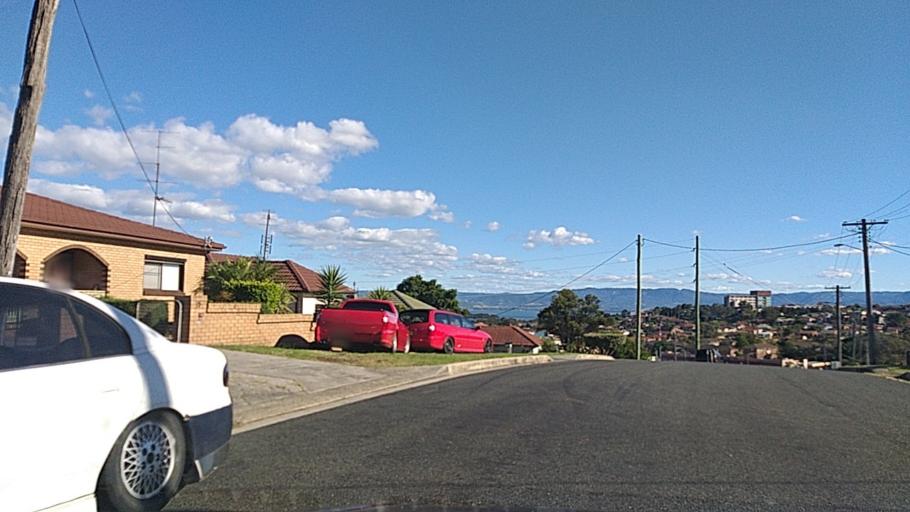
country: AU
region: New South Wales
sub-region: Wollongong
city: Port Kembla
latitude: -34.4812
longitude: 150.8905
